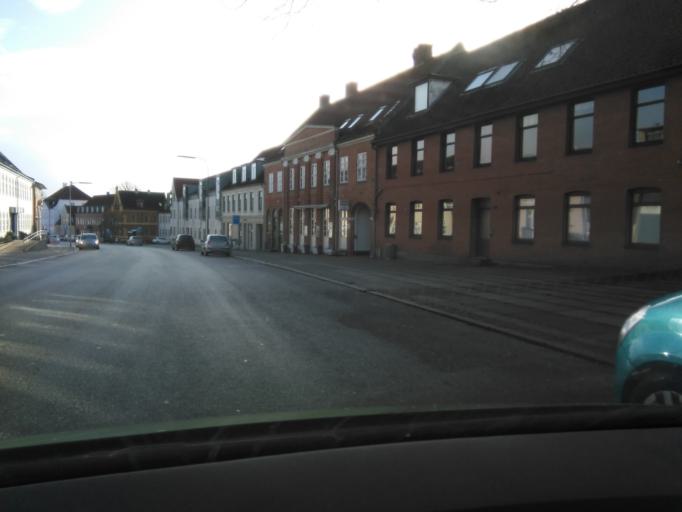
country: DK
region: Central Jutland
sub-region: Skanderborg Kommune
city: Skanderborg
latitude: 56.0318
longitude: 9.9325
